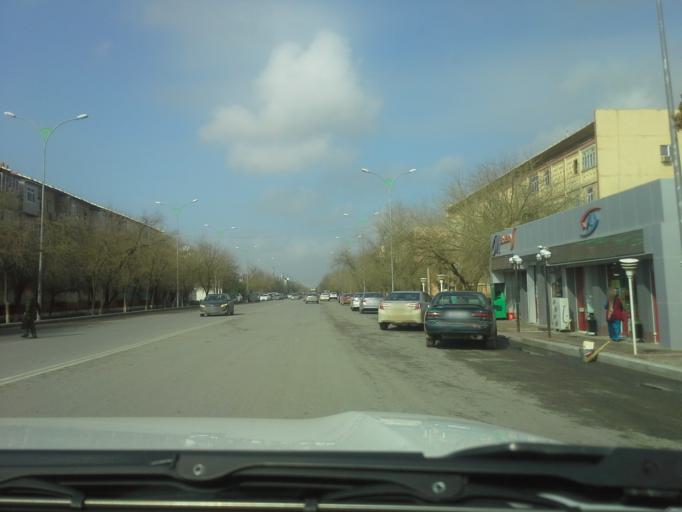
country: TM
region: Mary
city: Mary
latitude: 37.5923
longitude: 61.8336
